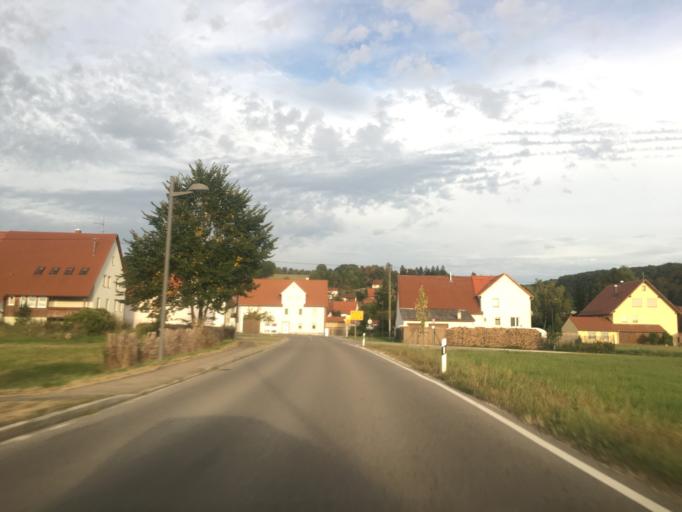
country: DE
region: Baden-Wuerttemberg
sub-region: Tuebingen Region
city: Gomadingen
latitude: 48.4316
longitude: 9.3762
